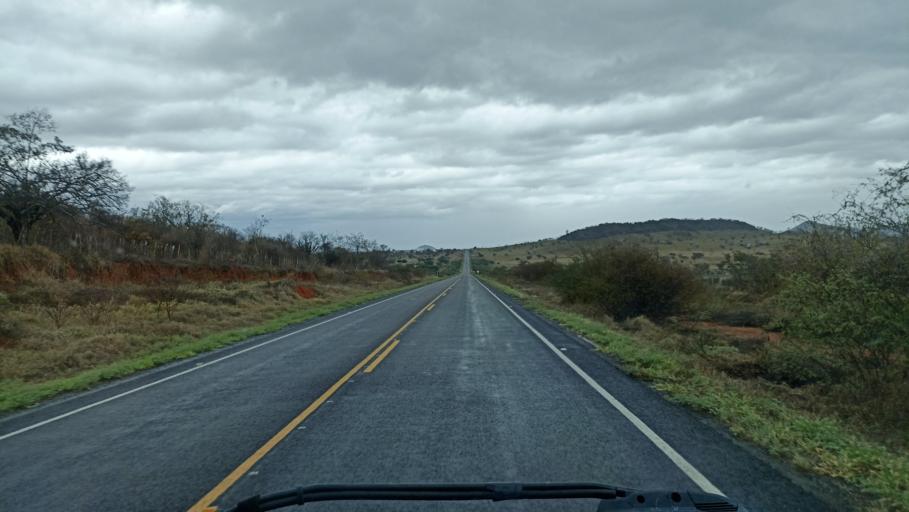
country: BR
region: Bahia
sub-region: Iacu
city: Iacu
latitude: -12.9606
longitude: -40.4779
